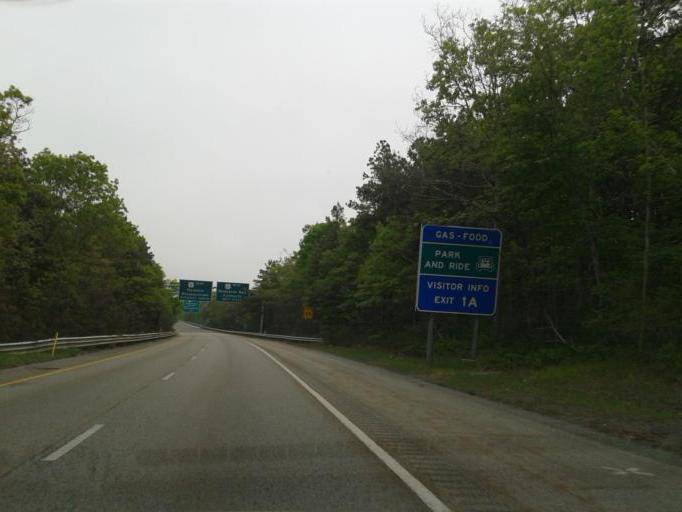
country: US
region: Massachusetts
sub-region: Barnstable County
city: Sagamore
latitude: 41.7872
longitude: -70.5451
